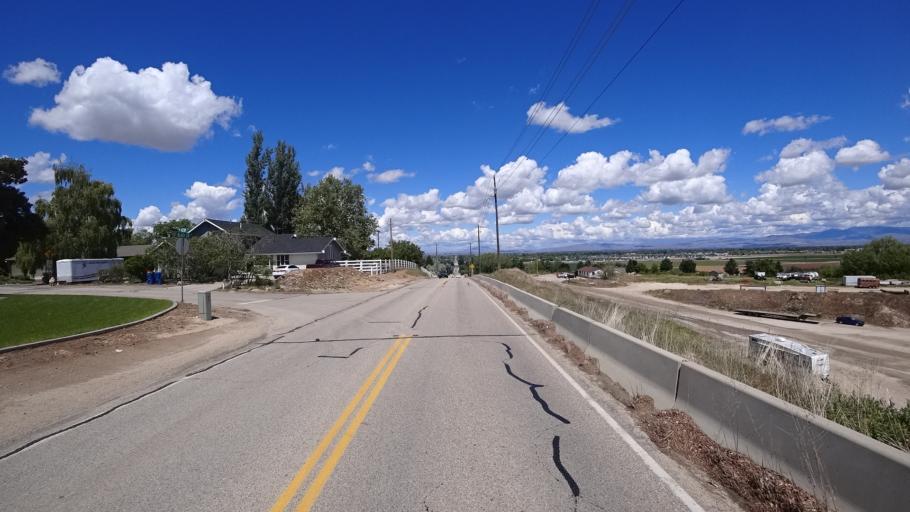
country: US
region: Idaho
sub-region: Ada County
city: Meridian
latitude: 43.5915
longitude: -116.4537
